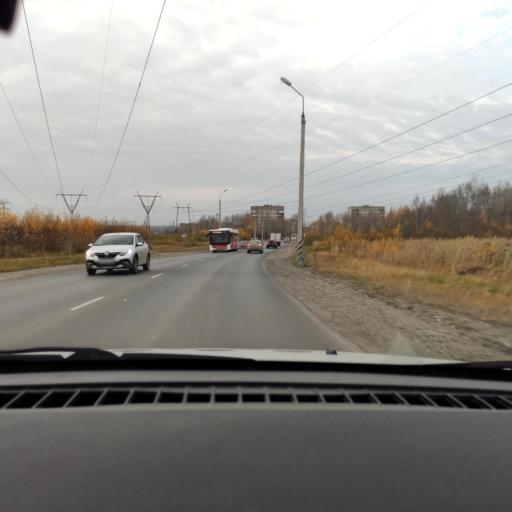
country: RU
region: Perm
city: Perm
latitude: 58.0993
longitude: 56.3926
